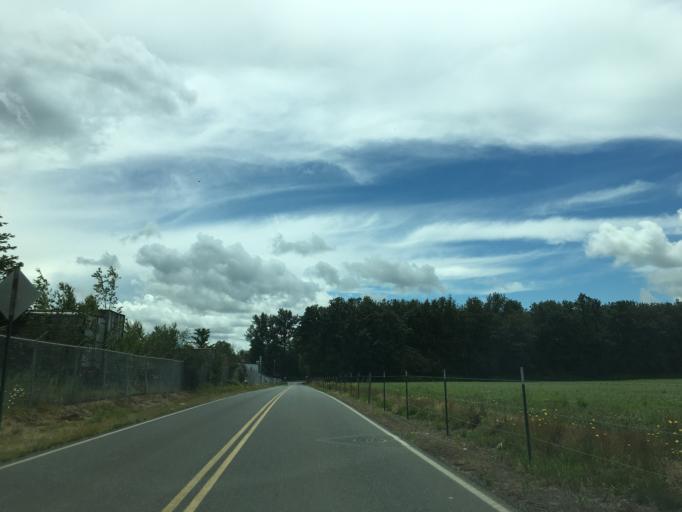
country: US
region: Washington
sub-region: Whatcom County
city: Lynden
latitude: 48.9384
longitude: -122.4959
